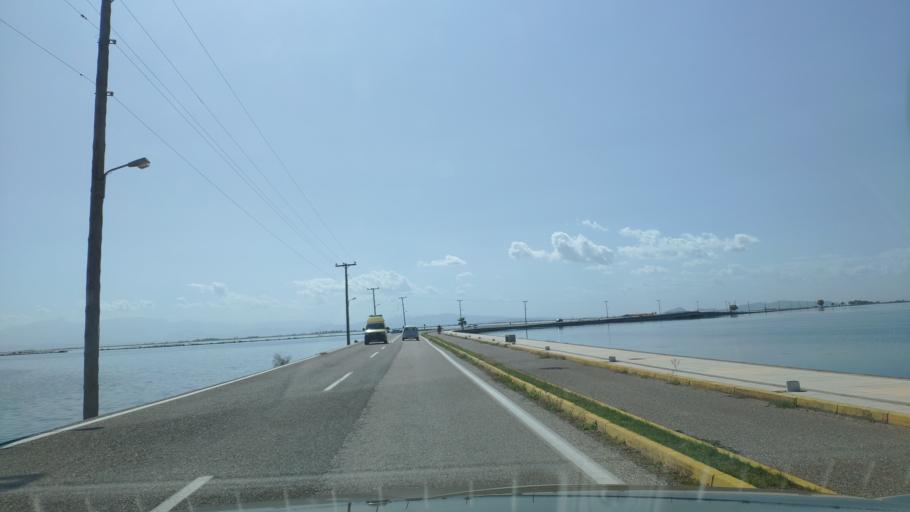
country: GR
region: West Greece
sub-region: Nomos Aitolias kai Akarnanias
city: Mesolongi
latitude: 38.3545
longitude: 21.4290
